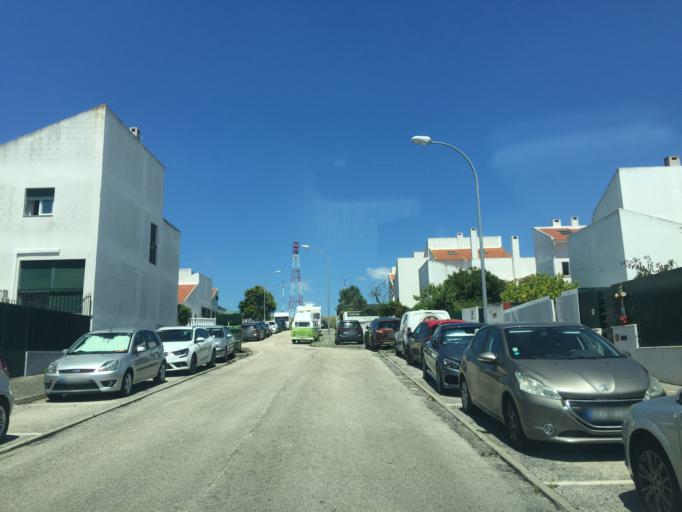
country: PT
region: Lisbon
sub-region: Oeiras
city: Quejas
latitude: 38.7238
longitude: -9.2677
